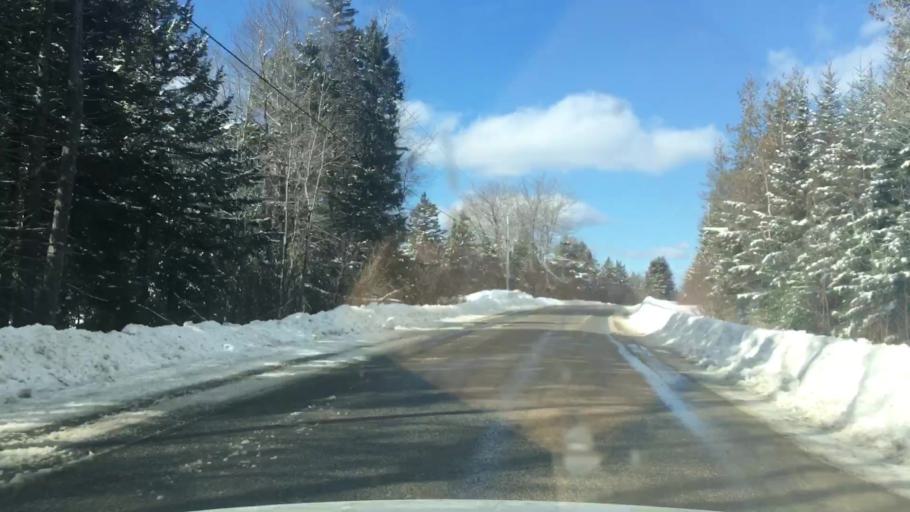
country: US
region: Maine
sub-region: Washington County
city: Machias
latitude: 44.6803
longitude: -67.4552
